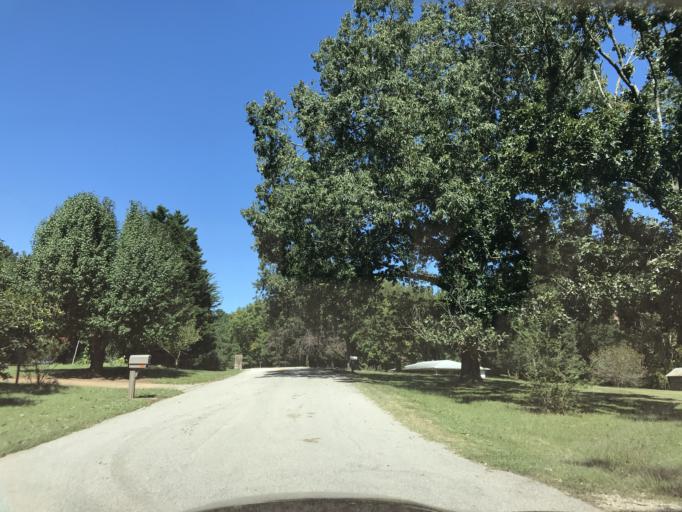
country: US
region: North Carolina
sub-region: Wake County
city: Wake Forest
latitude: 35.9460
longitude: -78.5902
